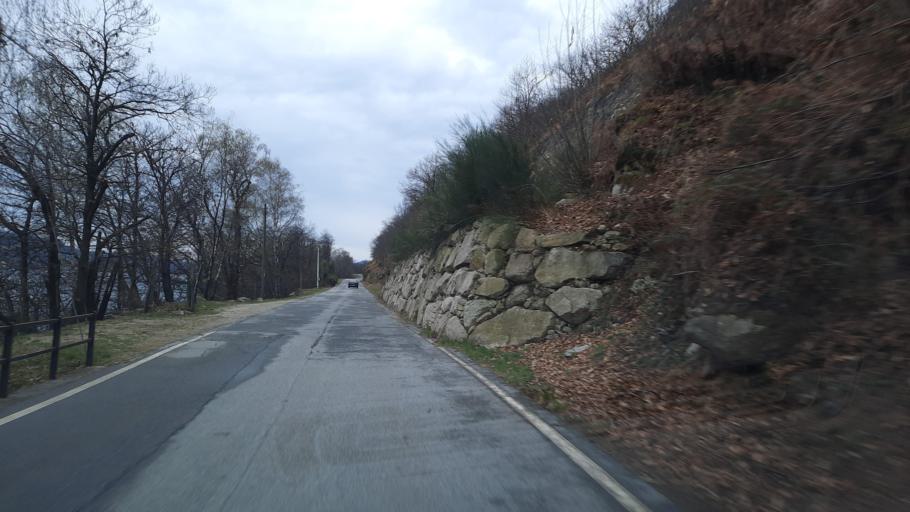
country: IT
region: Piedmont
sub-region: Provincia di Novara
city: Pella
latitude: 45.8178
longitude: 8.3843
